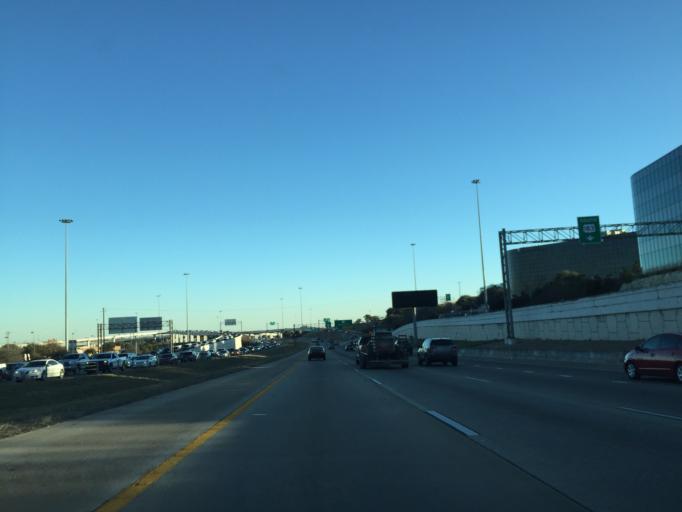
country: US
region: Texas
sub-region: Williamson County
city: Jollyville
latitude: 30.3860
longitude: -97.7435
